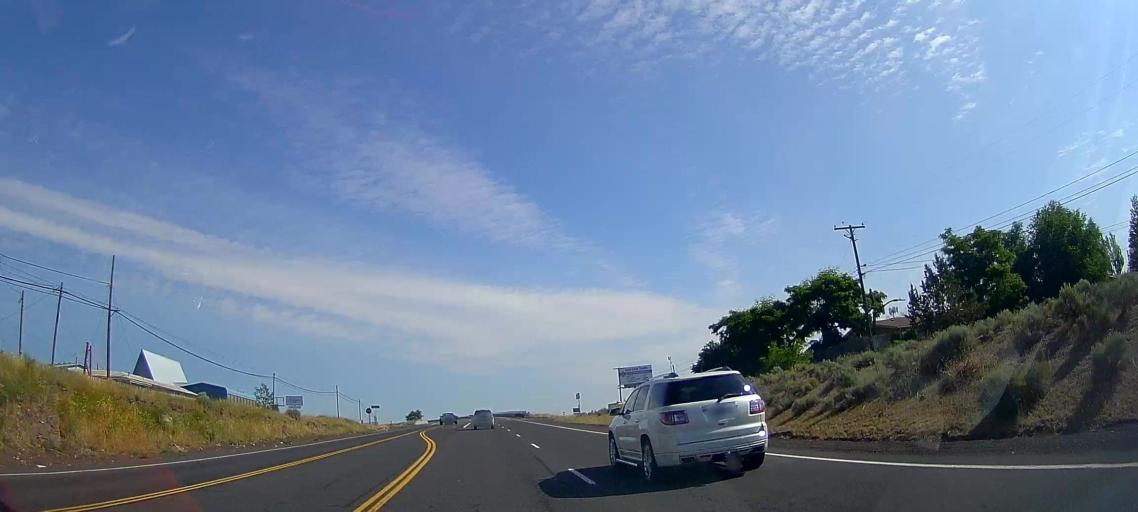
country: US
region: Oregon
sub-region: Jefferson County
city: Madras
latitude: 44.6512
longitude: -121.1285
